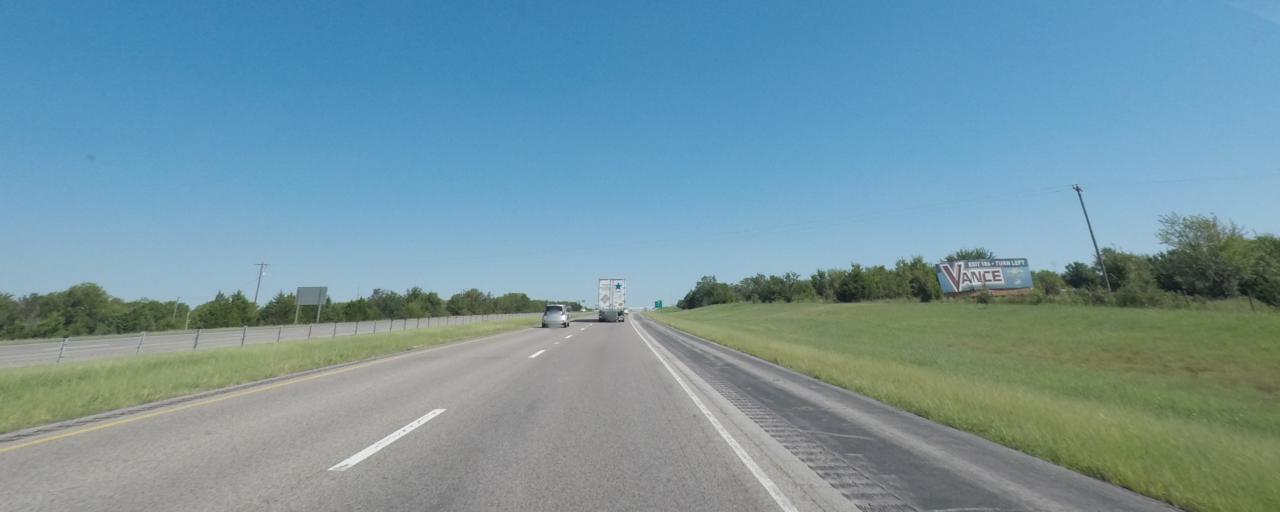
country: US
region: Oklahoma
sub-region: Noble County
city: Perry
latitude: 36.2660
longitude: -97.3273
